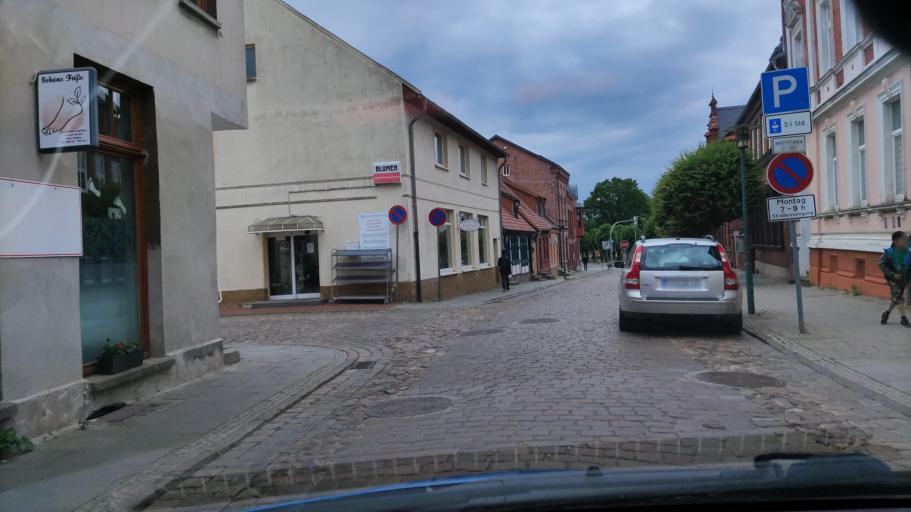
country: DE
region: Mecklenburg-Vorpommern
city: Plau am See
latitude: 53.4589
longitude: 12.2603
